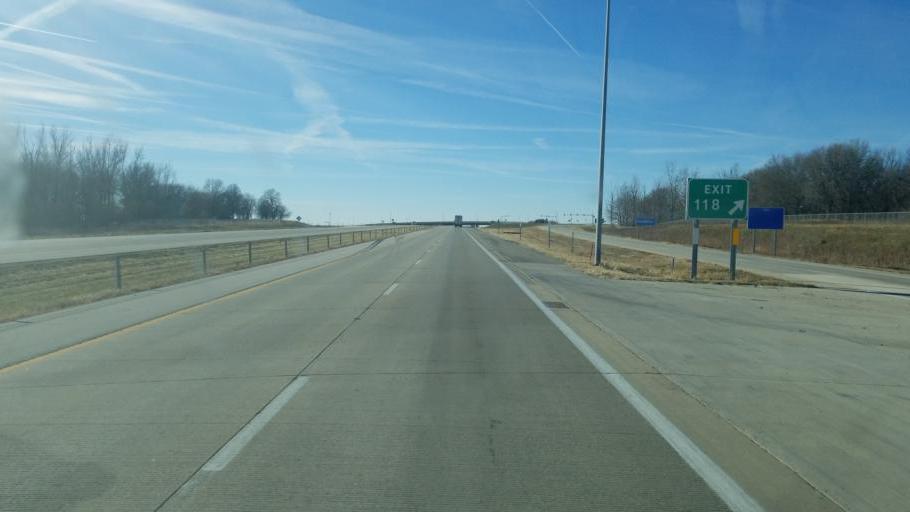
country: US
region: Iowa
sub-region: Dallas County
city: Waukee
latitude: 41.5728
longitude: -93.8470
